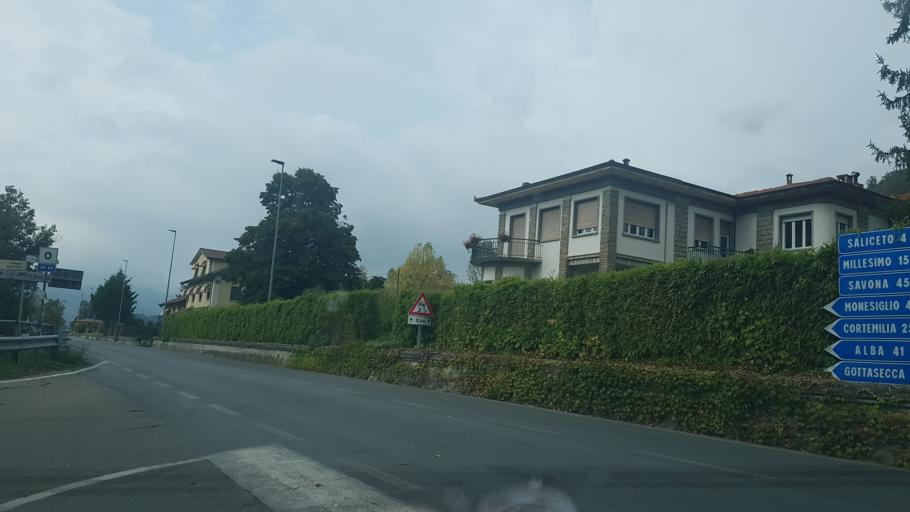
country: IT
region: Piedmont
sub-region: Provincia di Cuneo
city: Camerana
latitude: 44.4381
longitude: 8.1524
